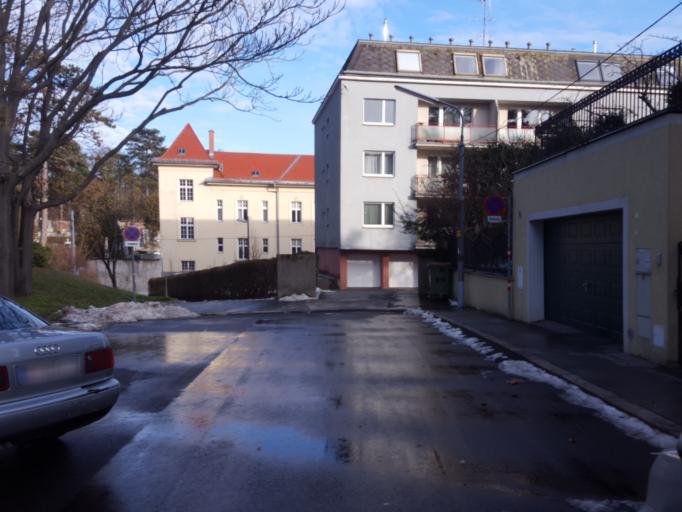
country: AT
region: Lower Austria
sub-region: Politischer Bezirk Modling
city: Perchtoldsdorf
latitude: 48.1779
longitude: 16.2973
